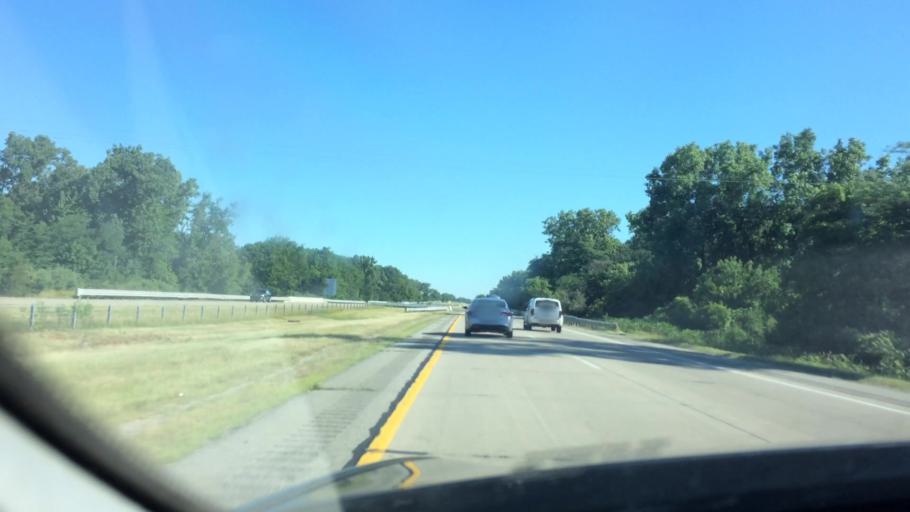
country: US
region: Michigan
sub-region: Monroe County
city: Dundee
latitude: 41.9787
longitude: -83.6782
